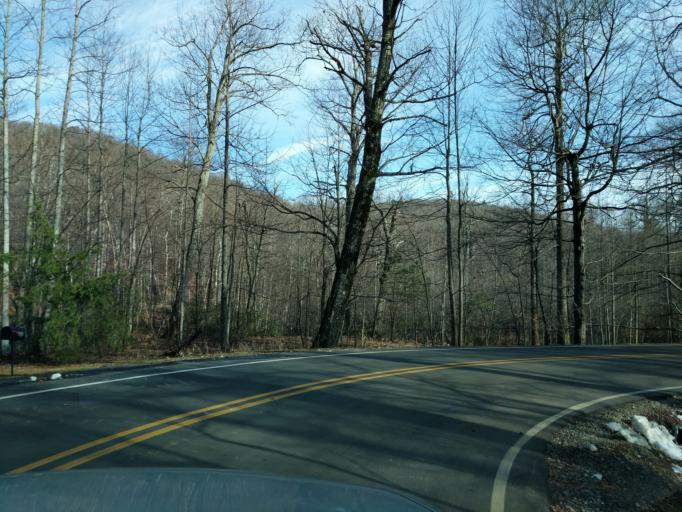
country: US
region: North Carolina
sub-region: Polk County
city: Columbus
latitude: 35.2797
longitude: -82.2203
